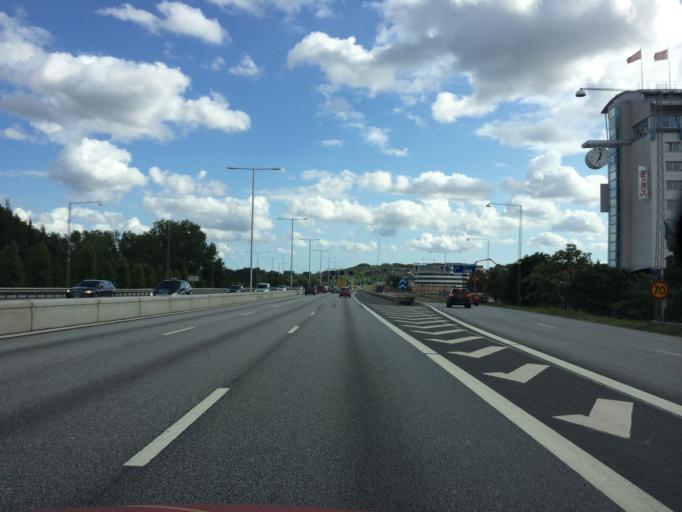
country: SE
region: Stockholm
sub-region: Solna Kommun
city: Solna
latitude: 59.3808
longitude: 18.0099
